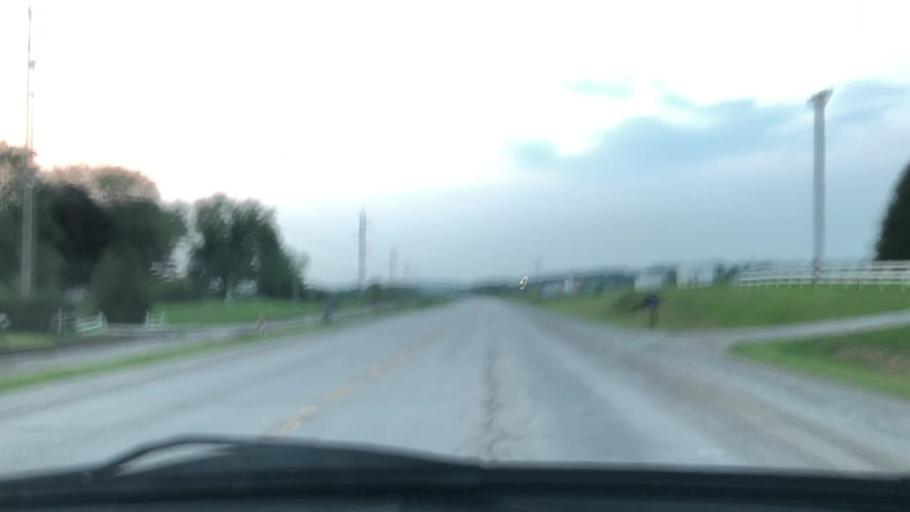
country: US
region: Iowa
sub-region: Johnson County
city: North Liberty
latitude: 41.7781
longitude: -91.6314
